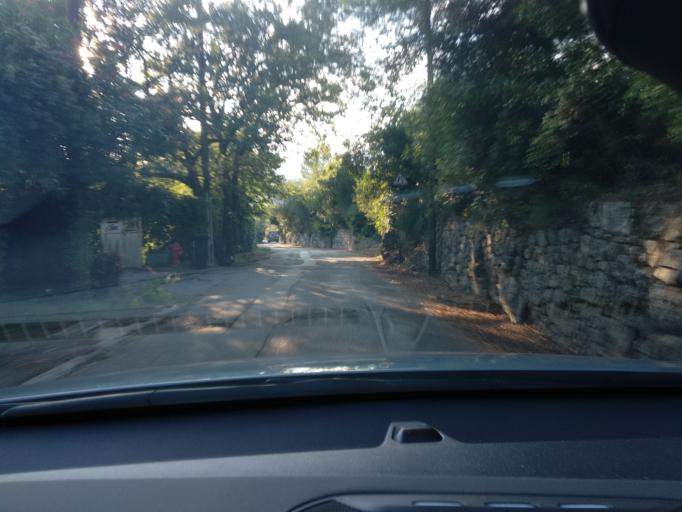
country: FR
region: Provence-Alpes-Cote d'Azur
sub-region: Departement des Alpes-Maritimes
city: Grasse
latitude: 43.6370
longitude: 6.9374
